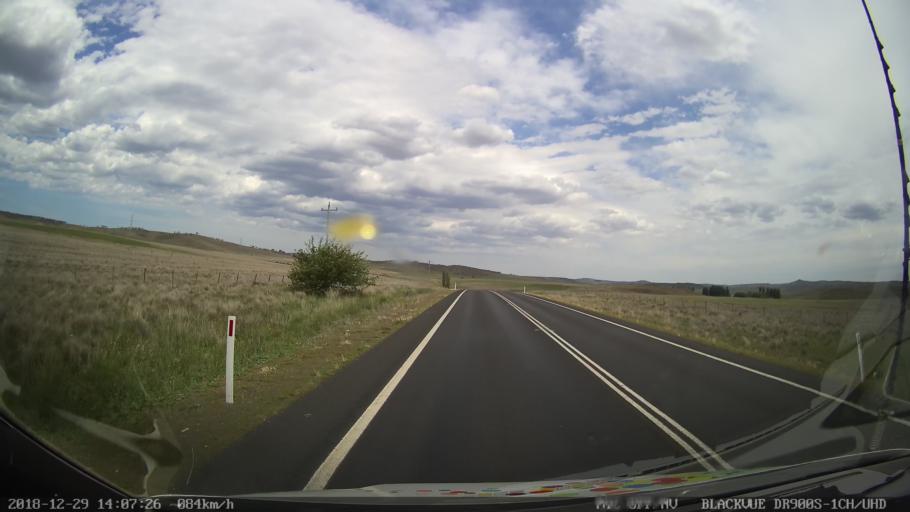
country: AU
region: New South Wales
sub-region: Cooma-Monaro
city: Cooma
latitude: -36.3517
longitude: 149.2137
